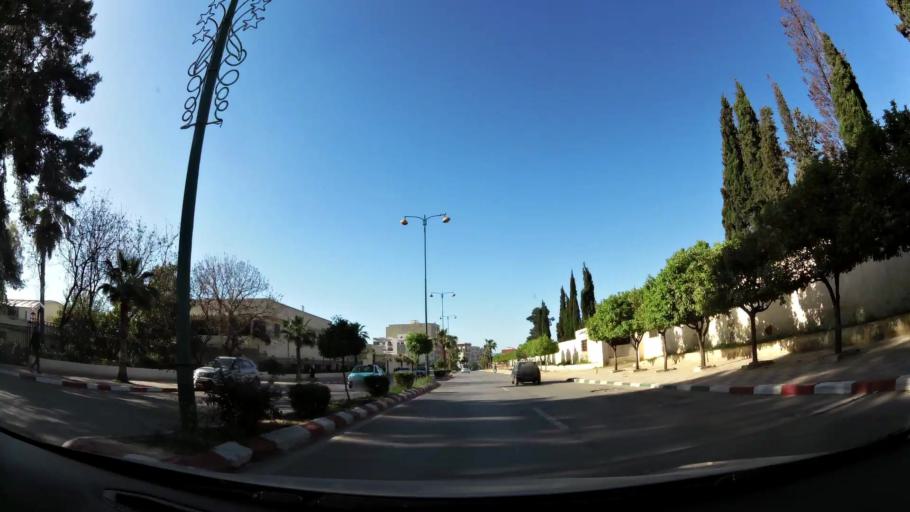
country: MA
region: Meknes-Tafilalet
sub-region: Meknes
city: Meknes
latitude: 33.8765
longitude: -5.5740
